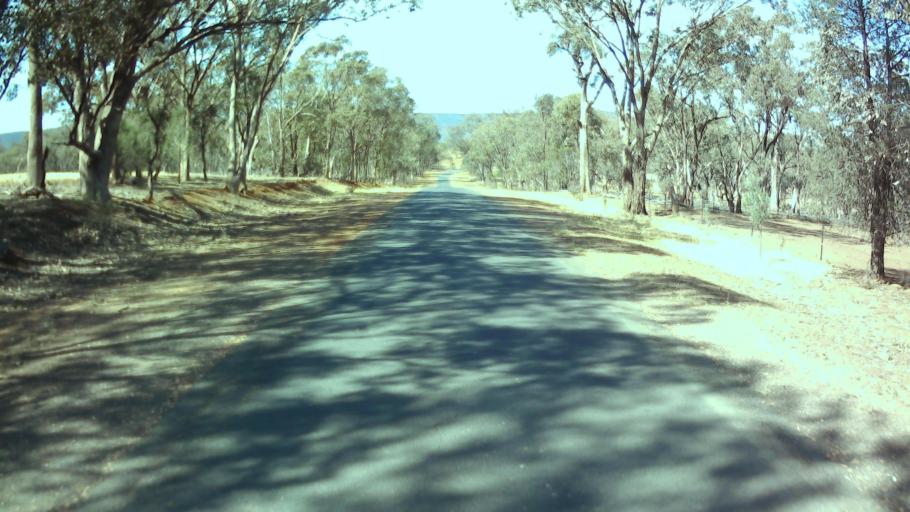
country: AU
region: New South Wales
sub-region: Weddin
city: Grenfell
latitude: -33.9368
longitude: 148.0812
